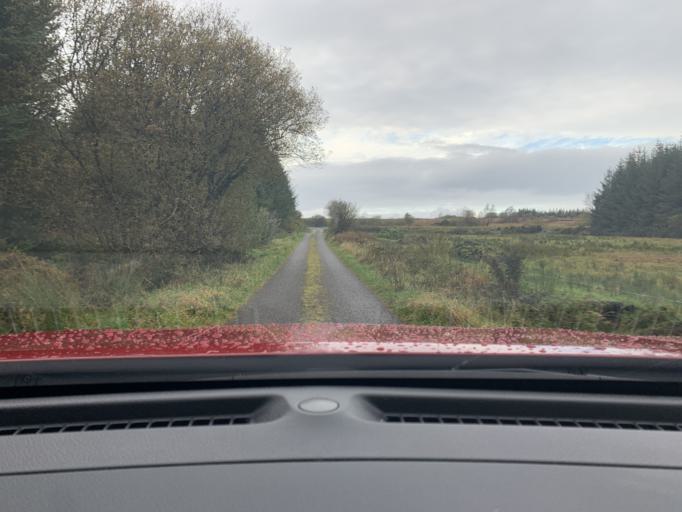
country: IE
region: Connaught
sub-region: Roscommon
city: Ballaghaderreen
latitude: 53.9215
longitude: -8.5701
